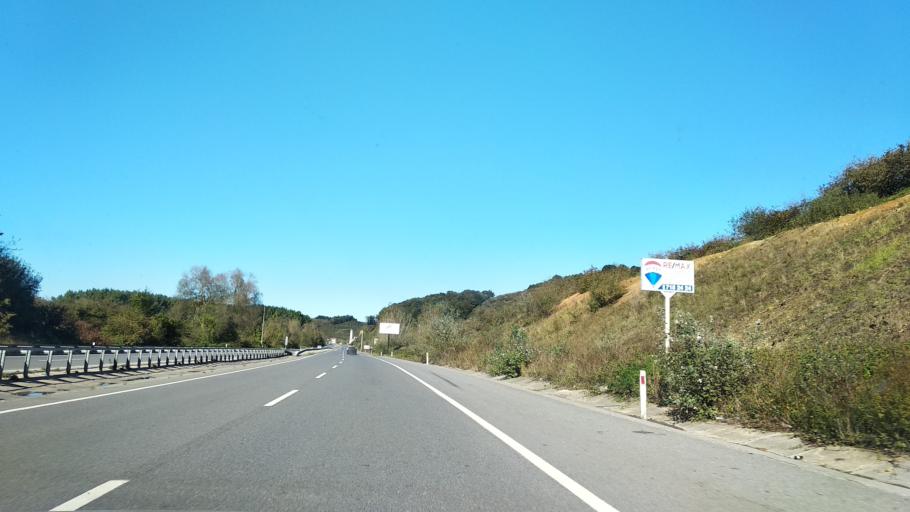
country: TR
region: Sakarya
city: Karasu
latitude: 41.0668
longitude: 30.6434
